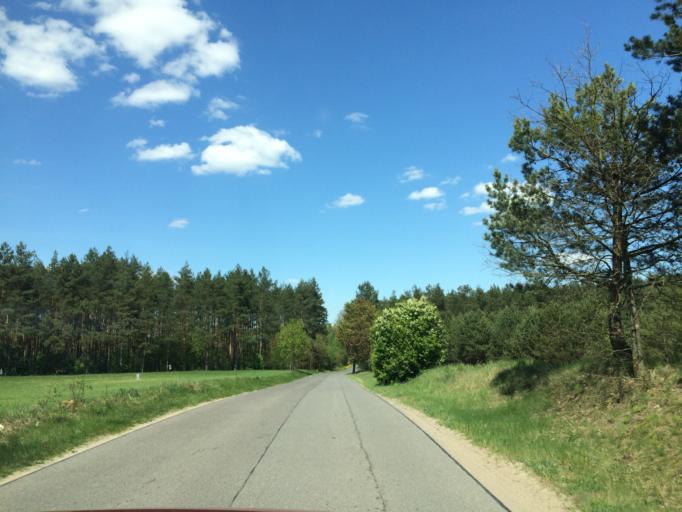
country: PL
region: Warmian-Masurian Voivodeship
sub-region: Powiat ilawski
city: Lubawa
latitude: 53.3920
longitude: 19.7364
